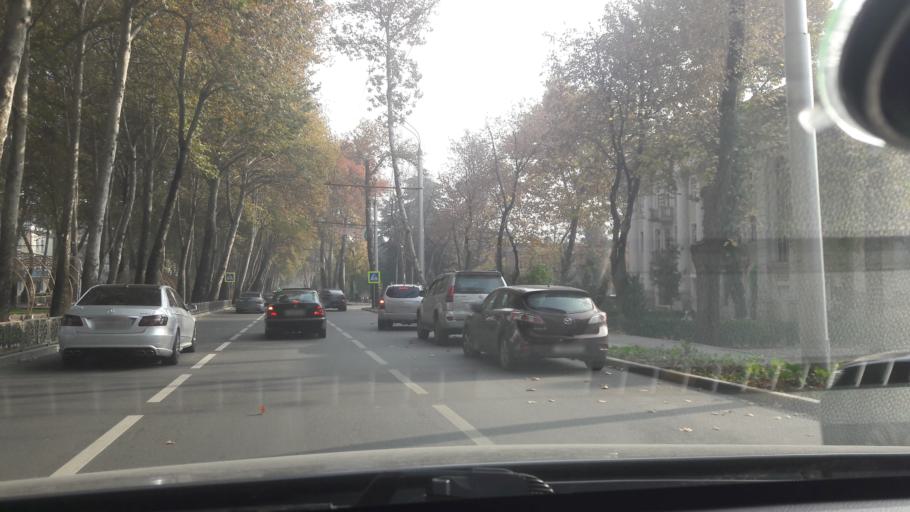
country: TJ
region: Dushanbe
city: Dushanbe
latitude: 38.5703
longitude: 68.7903
